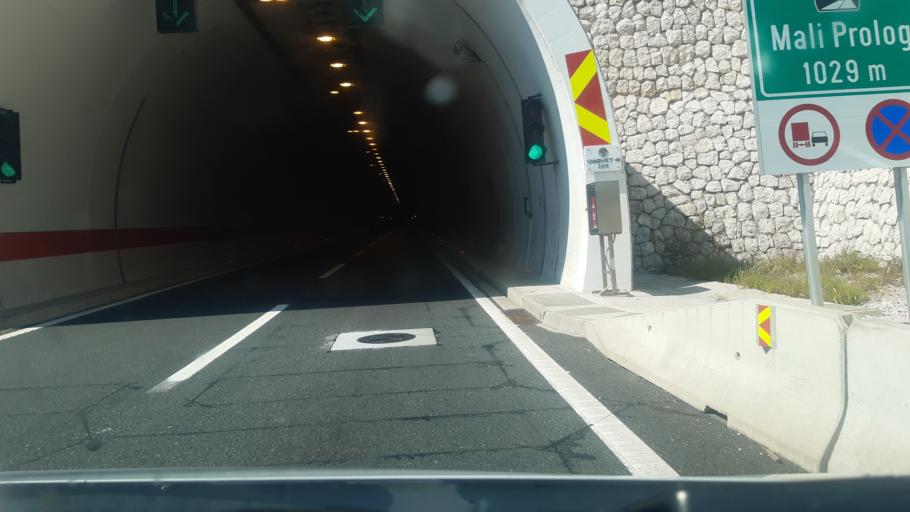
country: BA
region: Federation of Bosnia and Herzegovina
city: Ljubuski
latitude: 43.1441
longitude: 17.4880
